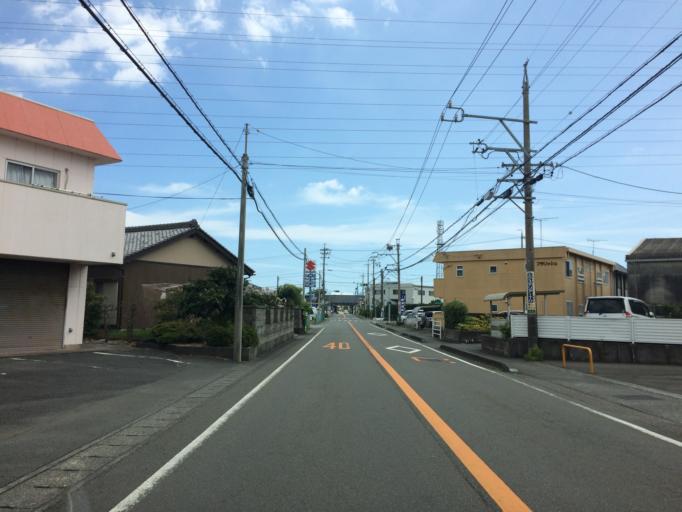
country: JP
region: Shizuoka
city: Yaizu
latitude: 34.8904
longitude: 138.3107
